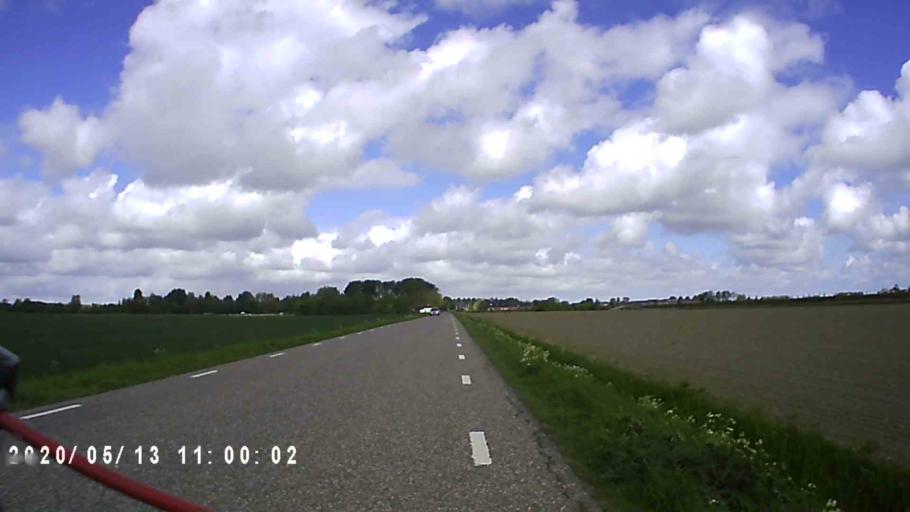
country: NL
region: Groningen
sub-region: Gemeente Zuidhorn
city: Grijpskerk
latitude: 53.2787
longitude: 6.3309
